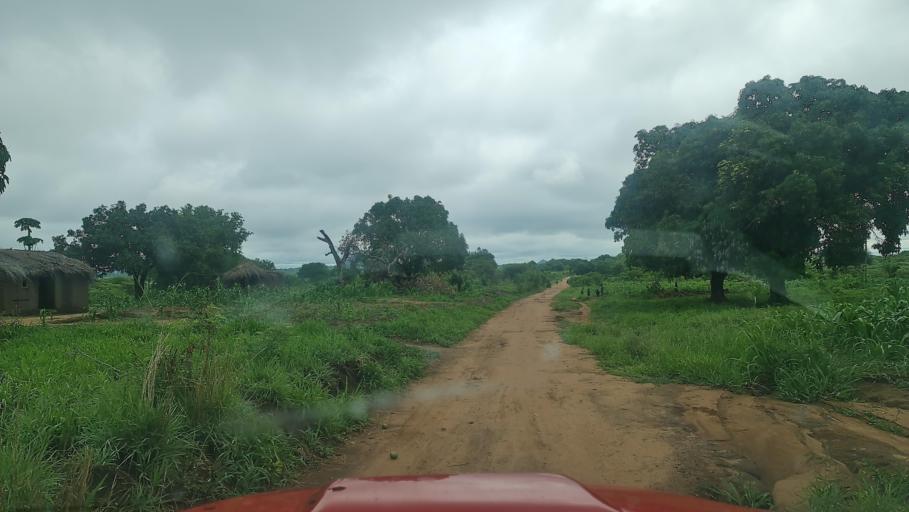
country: MW
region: Southern Region
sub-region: Nsanje District
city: Nsanje
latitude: -17.1935
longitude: 35.8484
